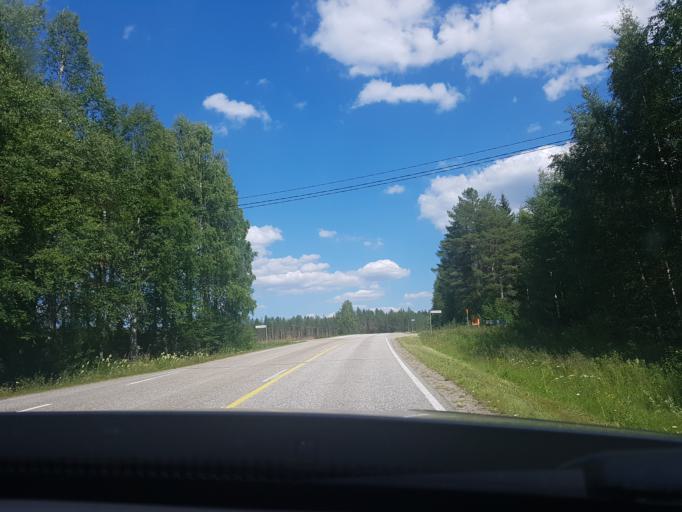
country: FI
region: Kainuu
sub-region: Kehys-Kainuu
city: Kuhmo
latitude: 64.2020
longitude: 29.6978
